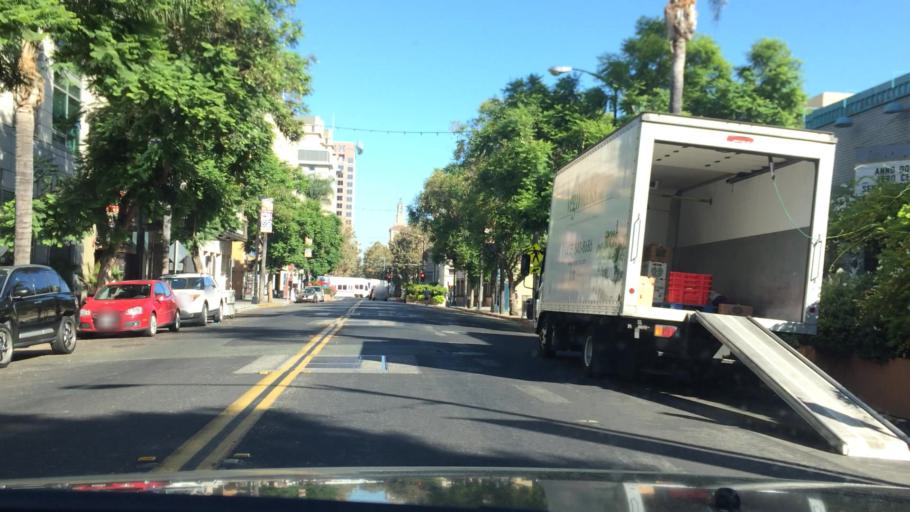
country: US
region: California
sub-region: Santa Clara County
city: San Jose
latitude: 37.3304
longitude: -121.8863
